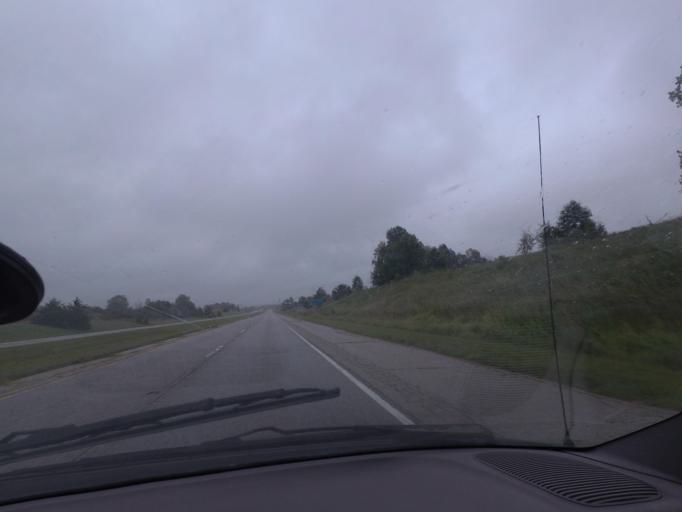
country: US
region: Illinois
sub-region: Pike County
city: Pittsfield
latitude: 39.6808
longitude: -90.8721
